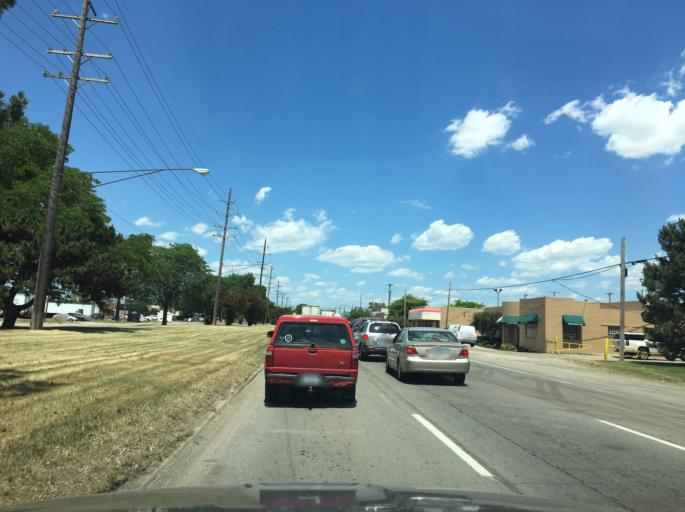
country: US
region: Michigan
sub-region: Macomb County
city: Warren
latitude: 42.4725
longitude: -83.0451
